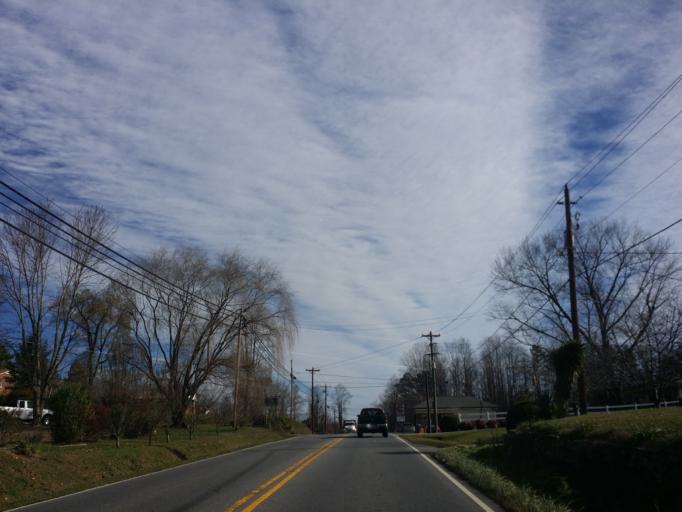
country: US
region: North Carolina
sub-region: McDowell County
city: West Marion
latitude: 35.6883
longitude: -82.0784
